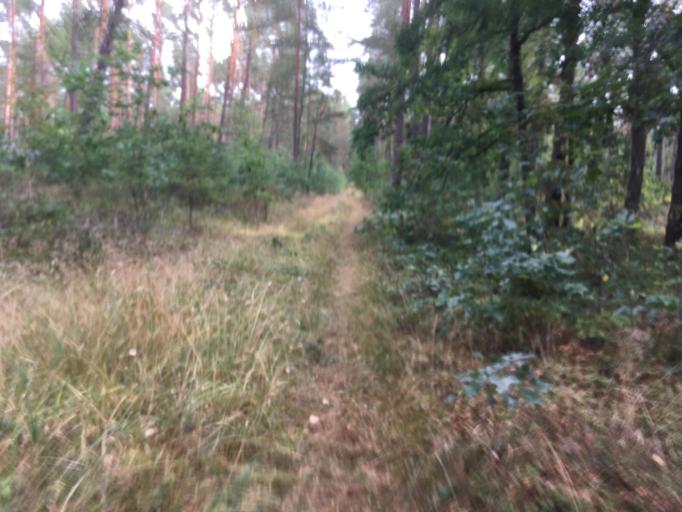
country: DE
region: Brandenburg
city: Friedrichswalde
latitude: 53.0083
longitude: 13.6056
